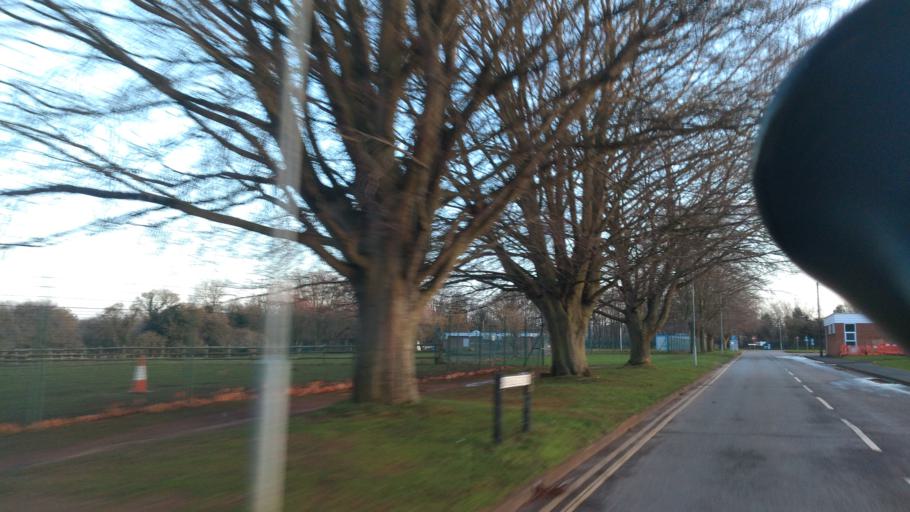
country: GB
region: England
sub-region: Oxfordshire
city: Shrivenham
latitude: 51.6053
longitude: -1.6355
